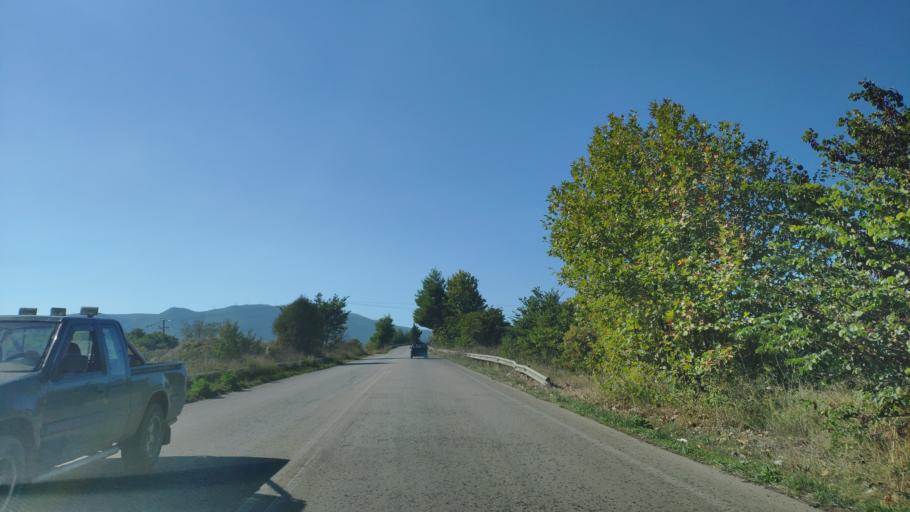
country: GR
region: Peloponnese
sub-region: Nomos Korinthias
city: Khiliomodhi
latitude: 37.8260
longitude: 22.8844
